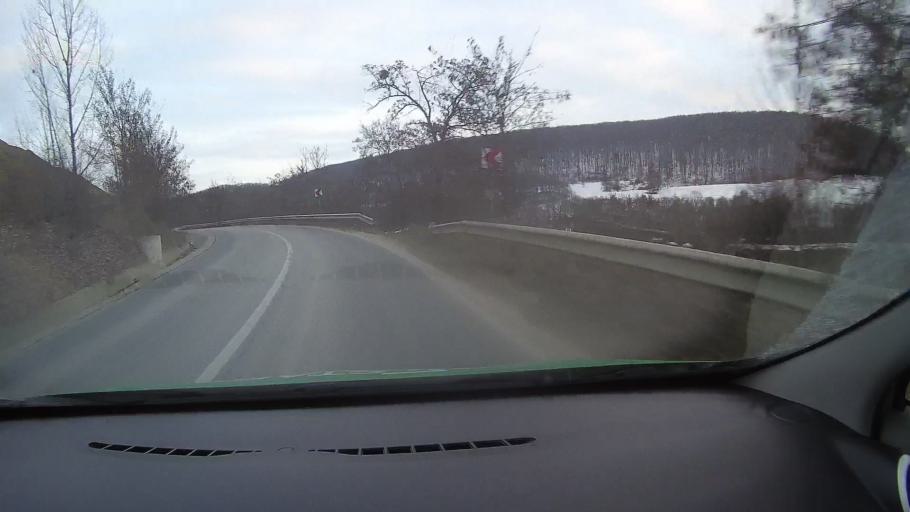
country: RO
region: Harghita
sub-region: Comuna Lupeni
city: Lupeni
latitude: 46.3589
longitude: 25.1899
